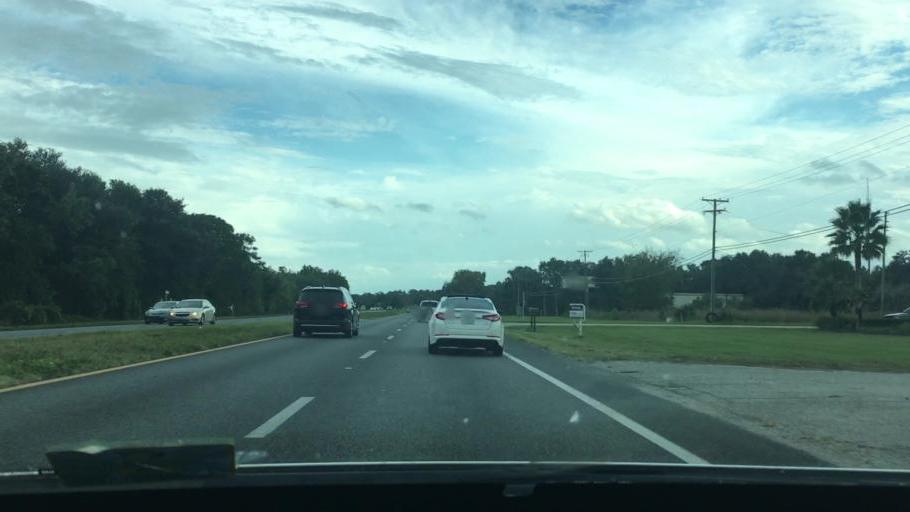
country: US
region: Florida
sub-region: Orange County
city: Bithlo
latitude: 28.5426
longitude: -81.0872
